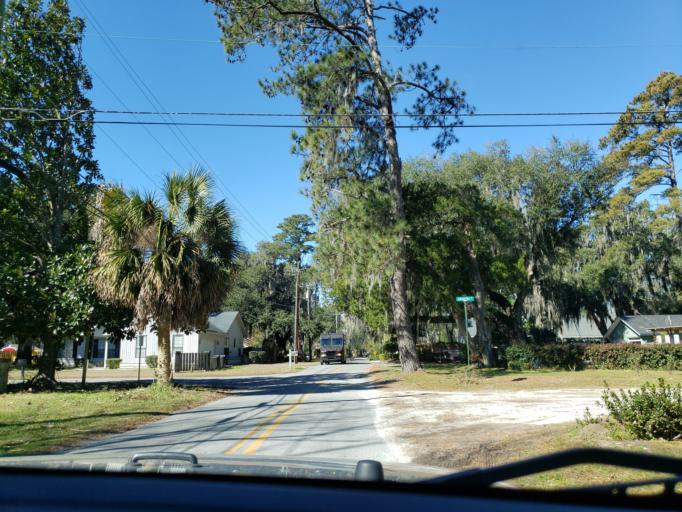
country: US
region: Georgia
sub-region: Chatham County
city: Whitemarsh Island
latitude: 32.0413
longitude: -80.9933
